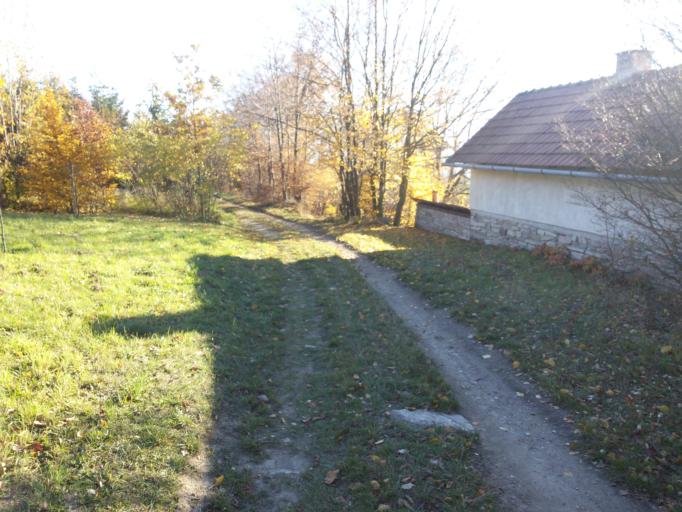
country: CZ
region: South Moravian
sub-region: Okres Brno-Venkov
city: Lomnice
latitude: 49.4006
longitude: 16.3843
